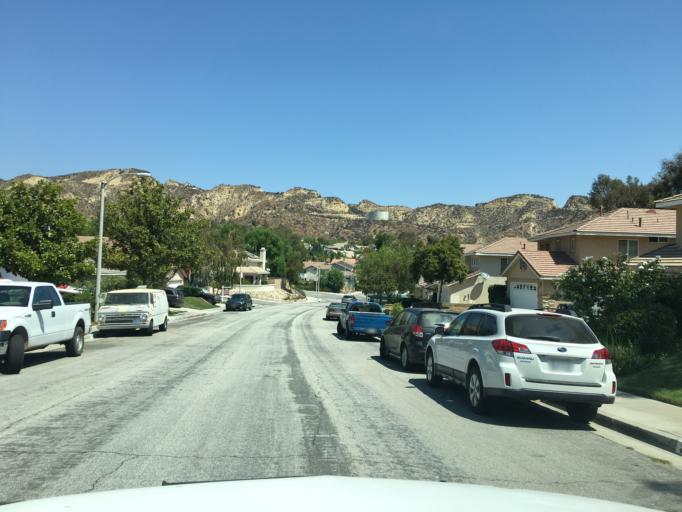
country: US
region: California
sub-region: Los Angeles County
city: Castaic
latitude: 34.4697
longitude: -118.6254
